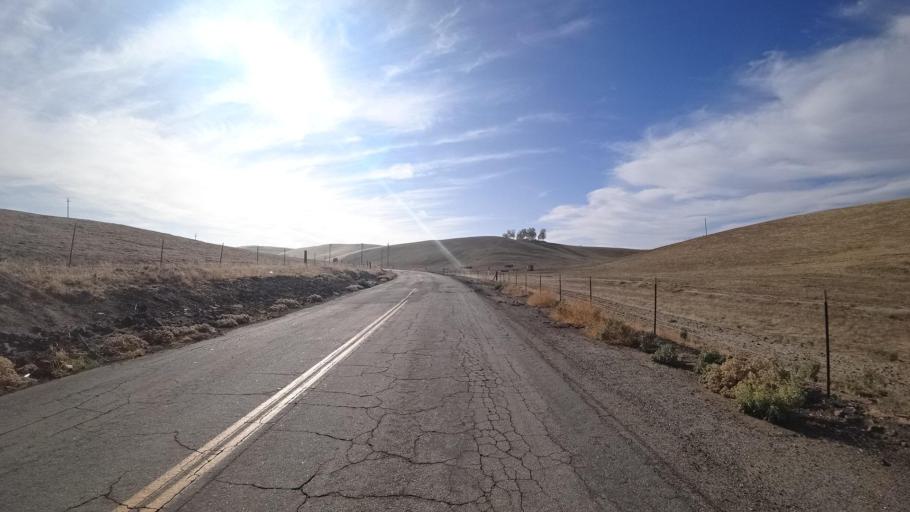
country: US
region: California
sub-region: Kern County
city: Oildale
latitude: 35.6187
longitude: -118.9870
